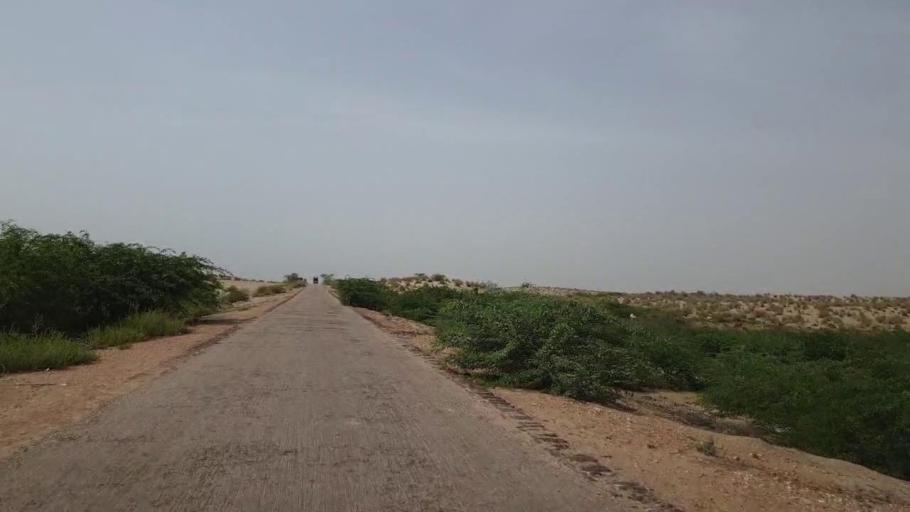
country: PK
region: Sindh
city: Bandhi
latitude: 26.5551
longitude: 68.3831
